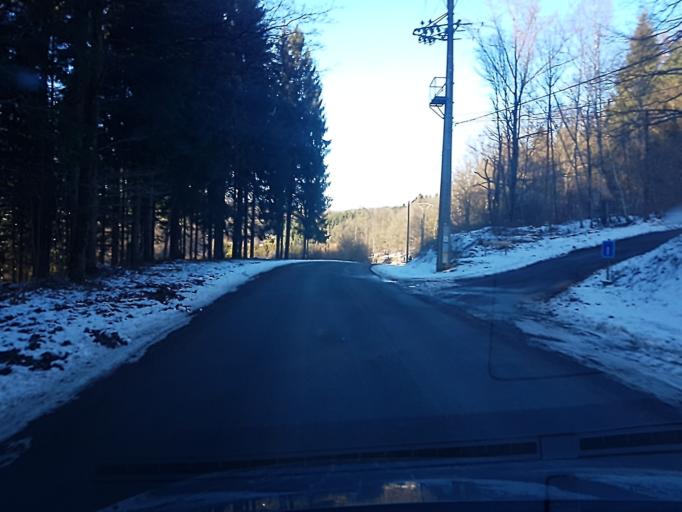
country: BE
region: Wallonia
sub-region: Province de Liege
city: Jalhay
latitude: 50.5402
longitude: 5.9682
